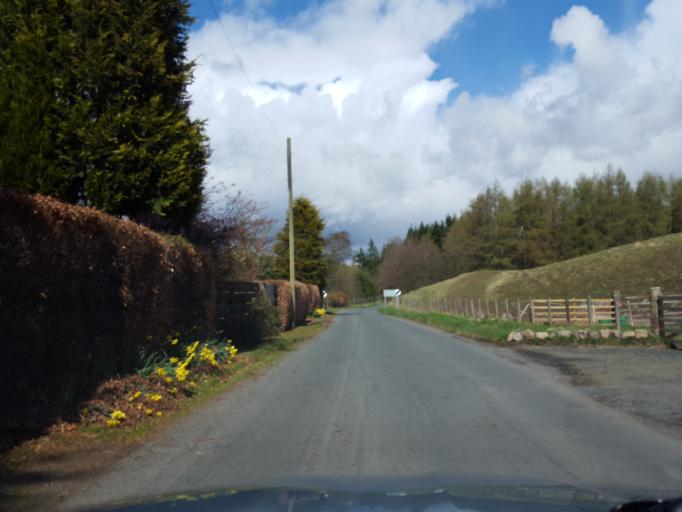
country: GB
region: Scotland
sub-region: Clackmannanshire
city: Dollar
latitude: 56.1997
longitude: -3.6038
